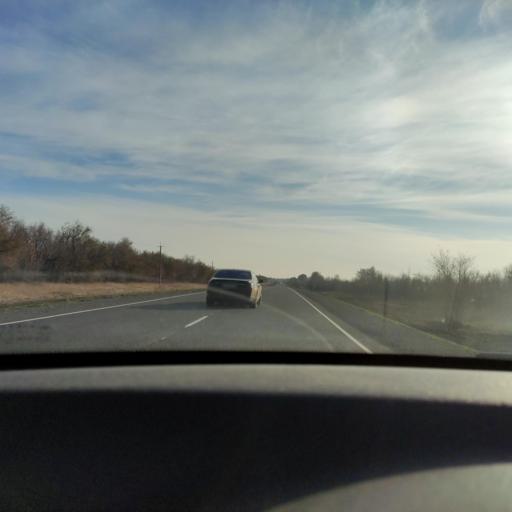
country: RU
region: Samara
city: Krasnoarmeyskoye
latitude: 52.8239
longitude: 50.0085
